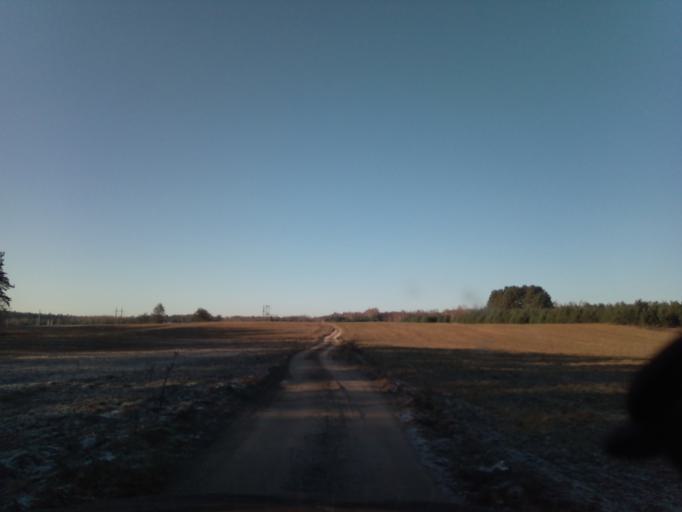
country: LT
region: Alytaus apskritis
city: Druskininkai
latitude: 53.9827
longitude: 23.9050
